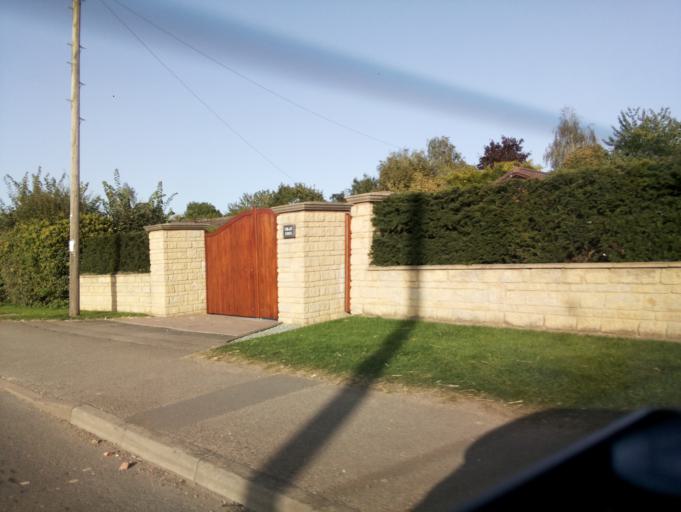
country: GB
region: England
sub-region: Gloucestershire
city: Newent
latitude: 51.9606
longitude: -2.3038
